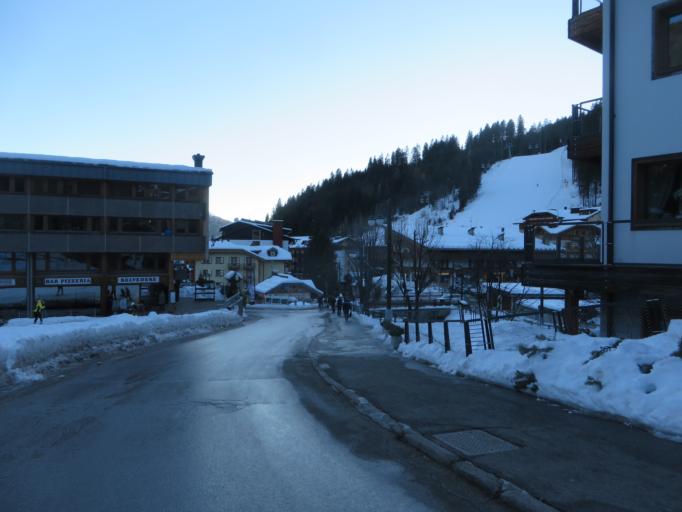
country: IT
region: Trentino-Alto Adige
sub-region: Provincia di Trento
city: Mezzana
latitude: 46.2325
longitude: 10.8273
